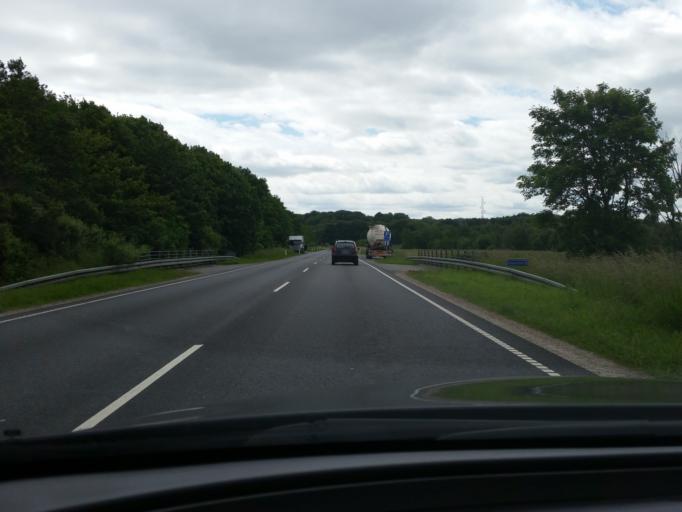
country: DK
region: Central Jutland
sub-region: Horsens Kommune
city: Horsens
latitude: 55.8847
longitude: 9.8266
